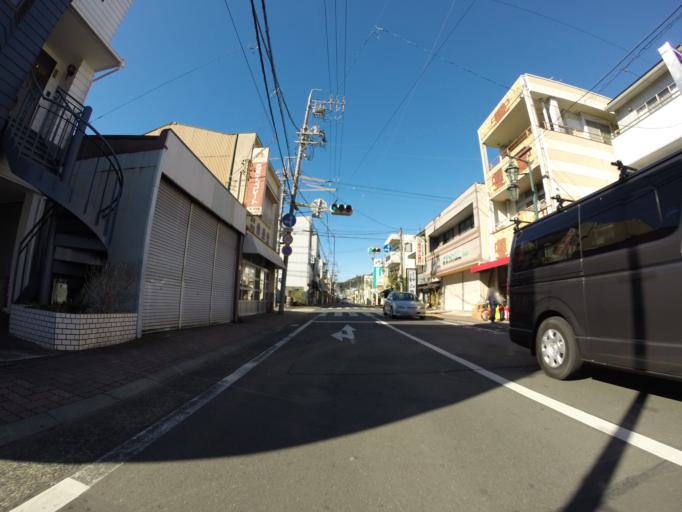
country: JP
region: Shizuoka
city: Shizuoka-shi
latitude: 34.9842
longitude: 138.3834
